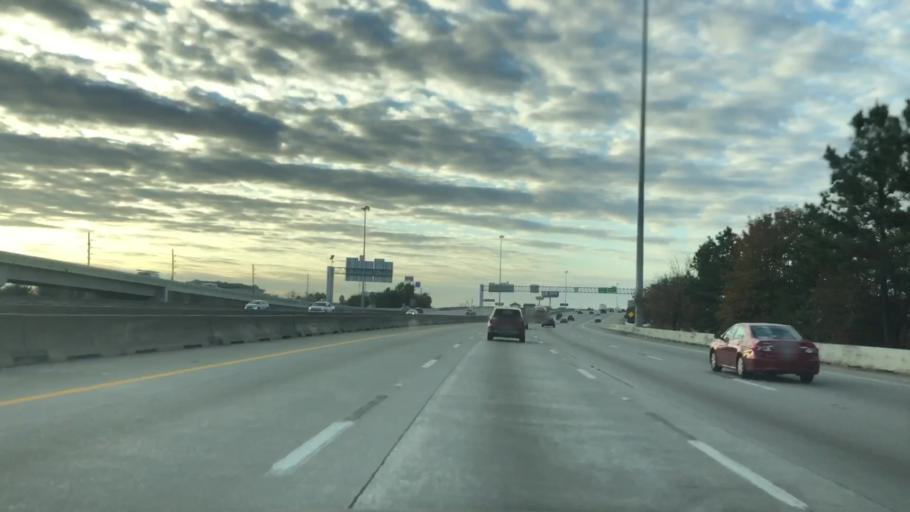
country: US
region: Texas
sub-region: Harris County
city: Aldine
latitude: 29.9362
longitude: -95.4126
